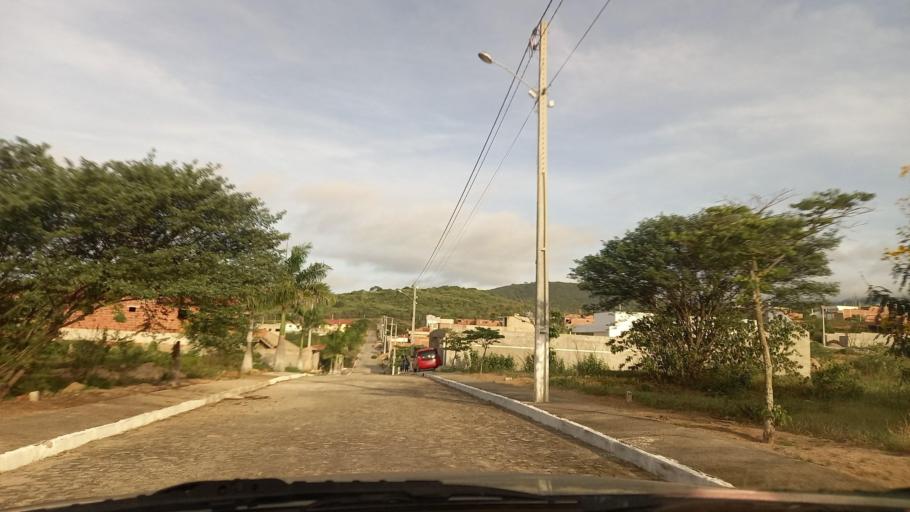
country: BR
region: Pernambuco
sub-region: Bezerros
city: Bezerros
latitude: -8.2169
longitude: -35.7485
